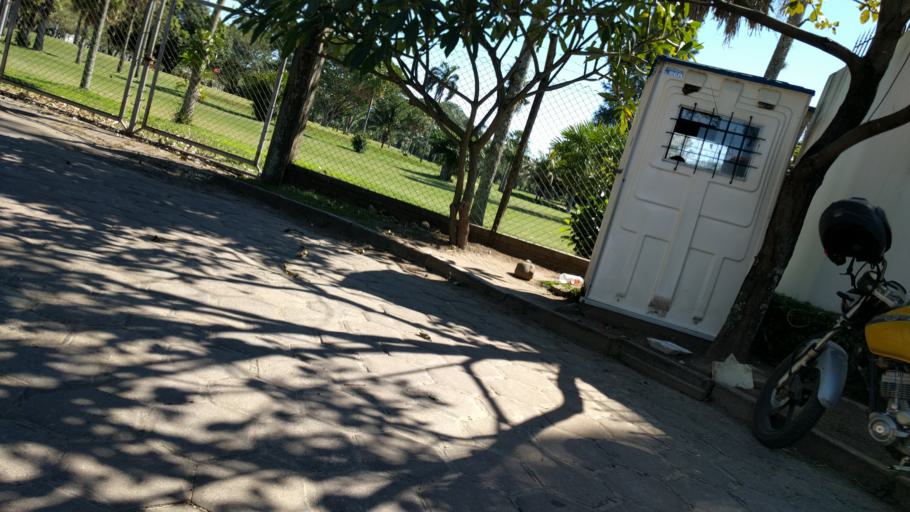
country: BO
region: Santa Cruz
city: Santa Cruz de la Sierra
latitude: -17.8037
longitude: -63.2085
